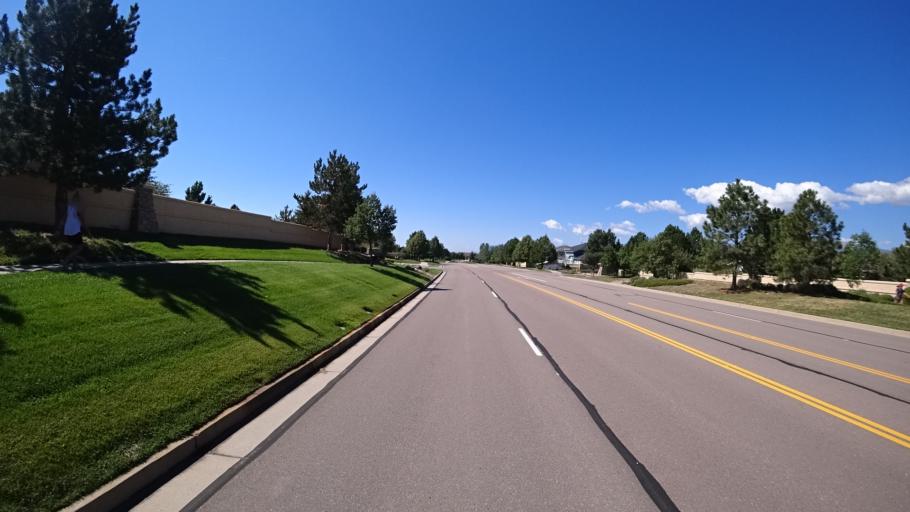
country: US
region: Colorado
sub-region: El Paso County
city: Black Forest
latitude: 38.9789
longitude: -104.7703
